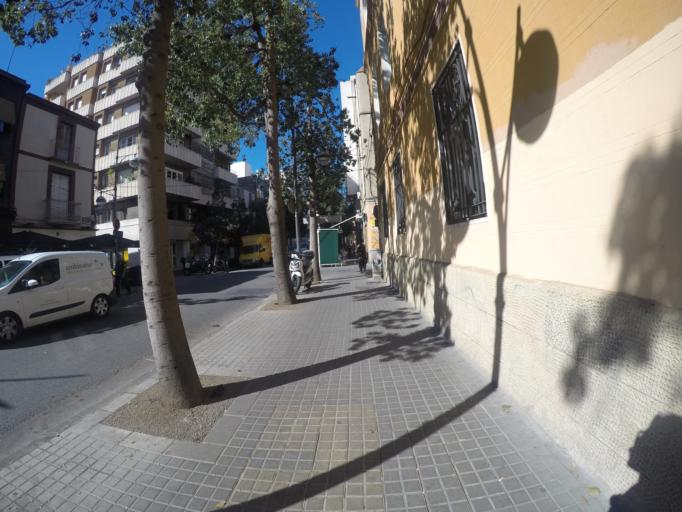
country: ES
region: Catalonia
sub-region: Provincia de Barcelona
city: Badalona
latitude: 41.4514
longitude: 2.2478
